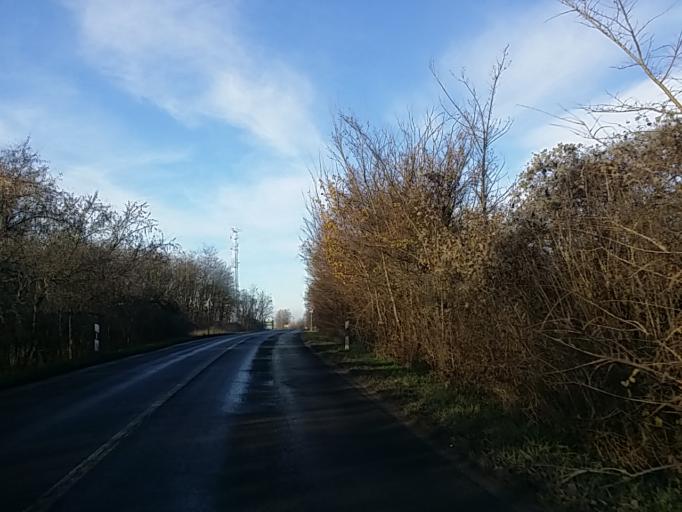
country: HU
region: Pest
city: Telki
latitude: 47.5373
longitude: 18.8467
